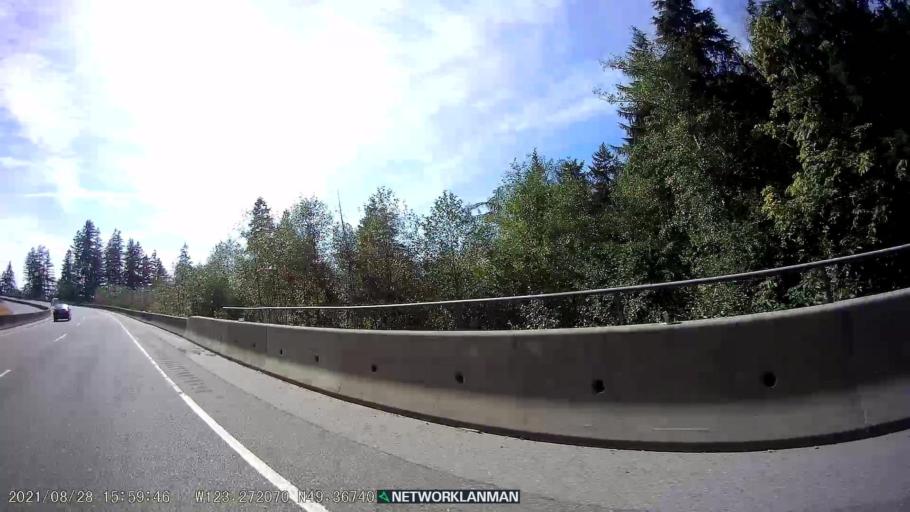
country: CA
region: British Columbia
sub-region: Greater Vancouver Regional District
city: Bowen Island
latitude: 49.3686
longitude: -123.2715
